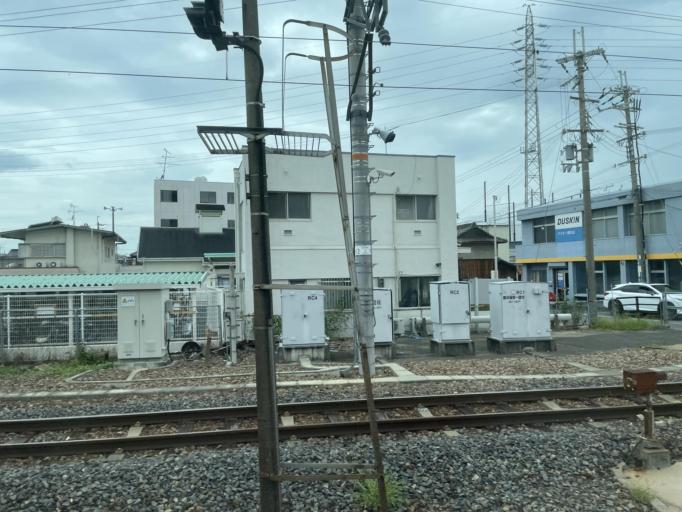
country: JP
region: Osaka
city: Kaizuka
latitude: 34.4395
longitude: 135.3720
